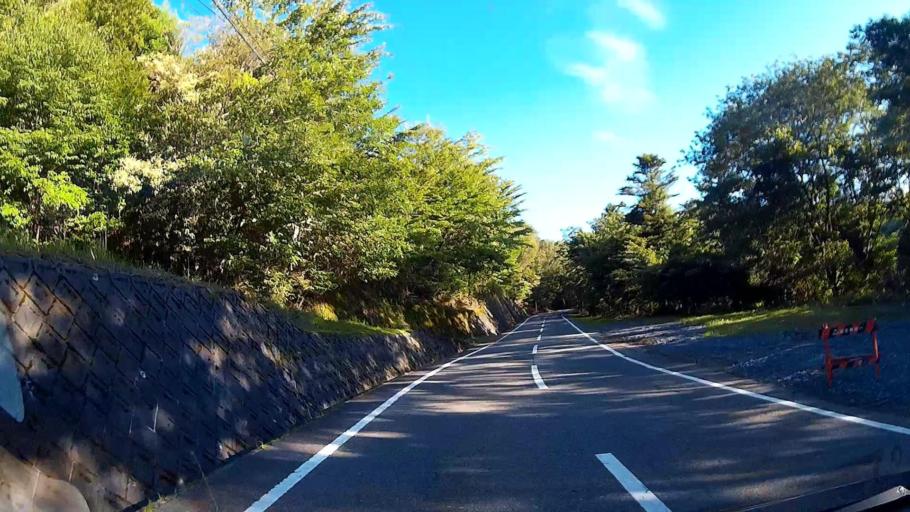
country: JP
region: Shizuoka
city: Shizuoka-shi
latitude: 35.1936
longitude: 138.2498
